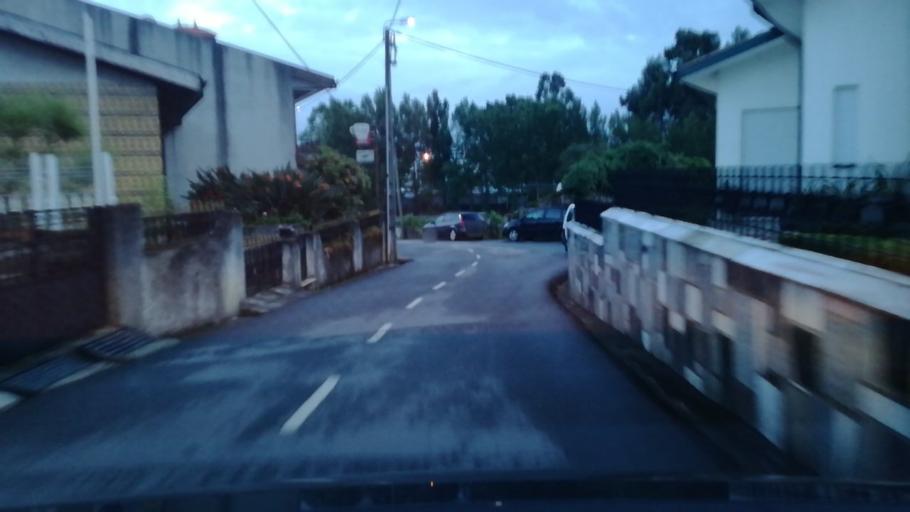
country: PT
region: Porto
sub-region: Maia
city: Anta
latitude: 41.2523
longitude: -8.6268
